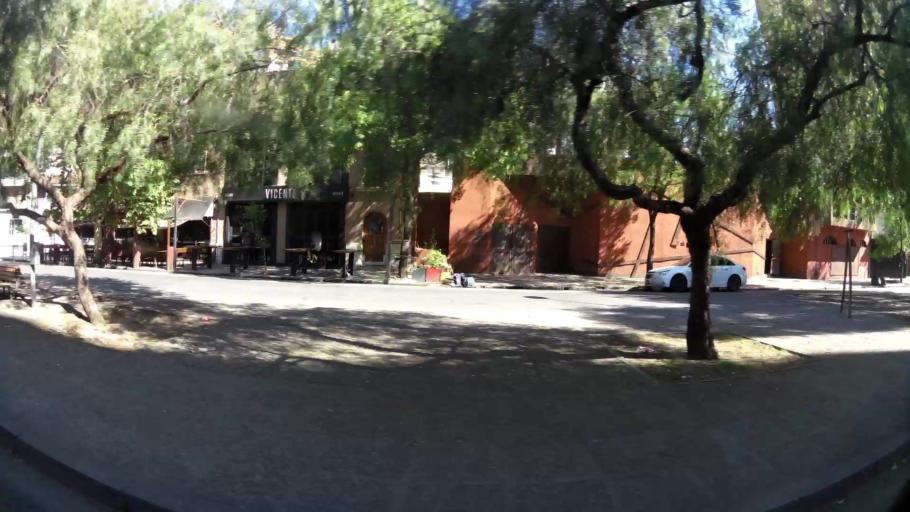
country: AR
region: Cordoba
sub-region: Departamento de Capital
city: Cordoba
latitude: -31.4292
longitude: -64.1861
